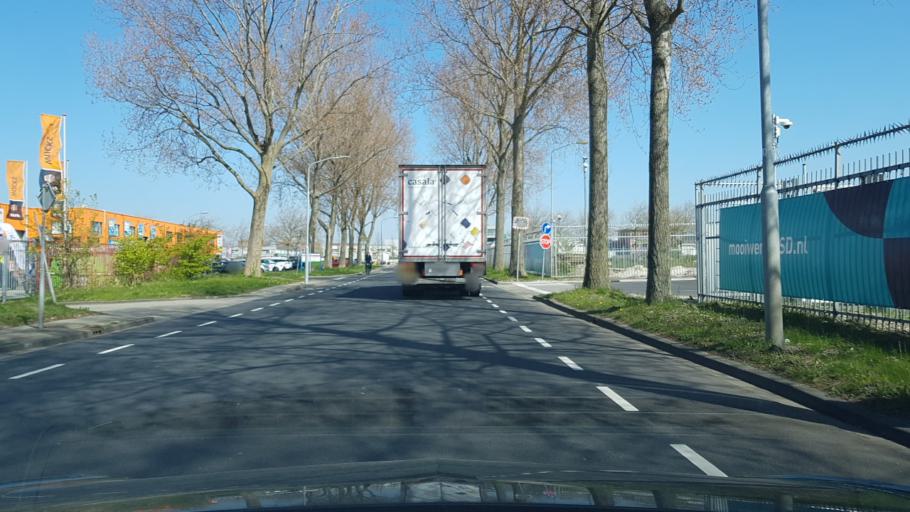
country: NL
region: North Holland
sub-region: Gemeente Haarlem
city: Haarlem
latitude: 52.3938
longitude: 4.6562
